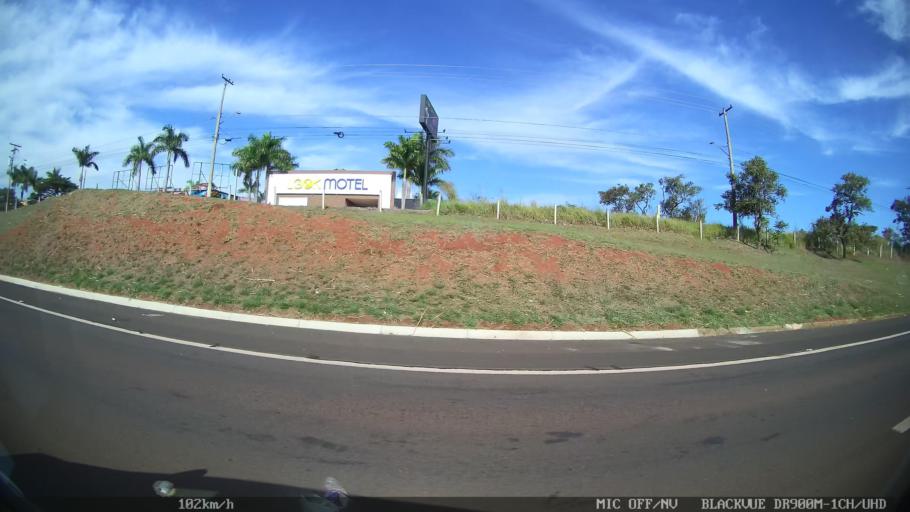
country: BR
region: Sao Paulo
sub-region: Araraquara
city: Araraquara
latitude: -21.7968
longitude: -48.1377
